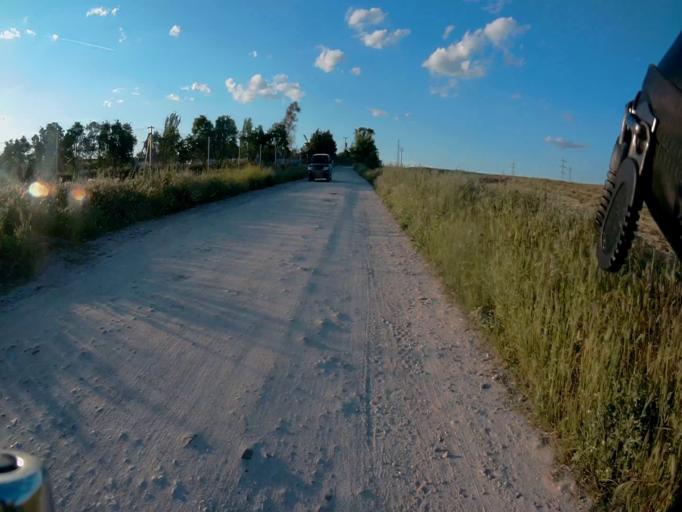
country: ES
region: Madrid
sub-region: Provincia de Madrid
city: Leganes
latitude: 40.3286
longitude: -3.7951
